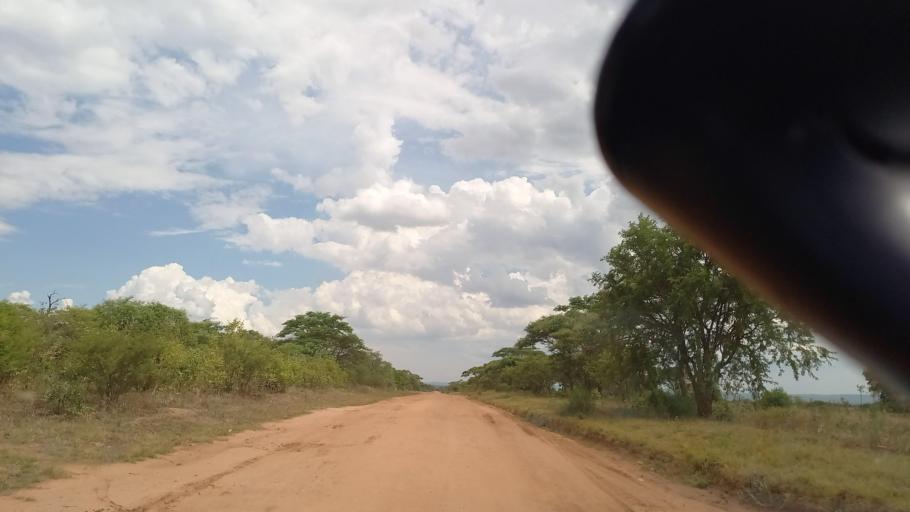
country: ZM
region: Southern
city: Nakambala
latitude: -16.0366
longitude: 27.9710
